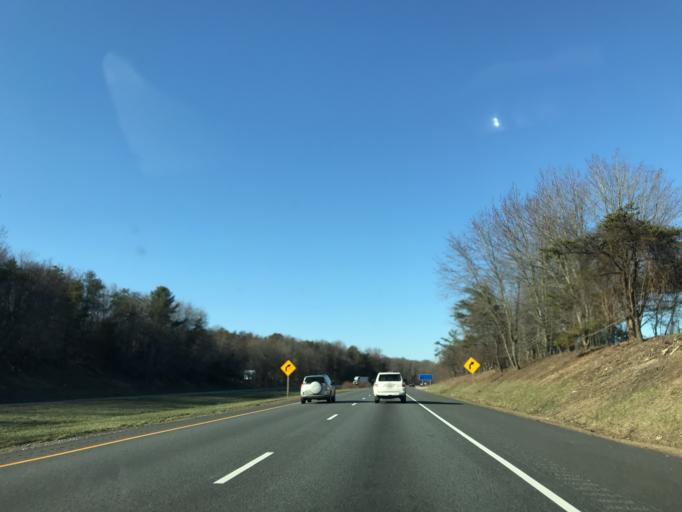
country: US
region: Pennsylvania
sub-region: York County
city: New Freedom
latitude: 39.6477
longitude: -76.6658
